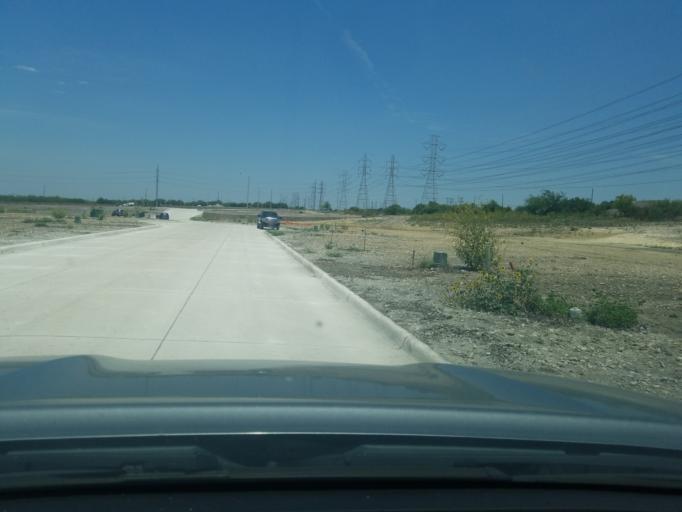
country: US
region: Texas
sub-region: Bexar County
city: Converse
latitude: 29.4650
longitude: -98.3246
